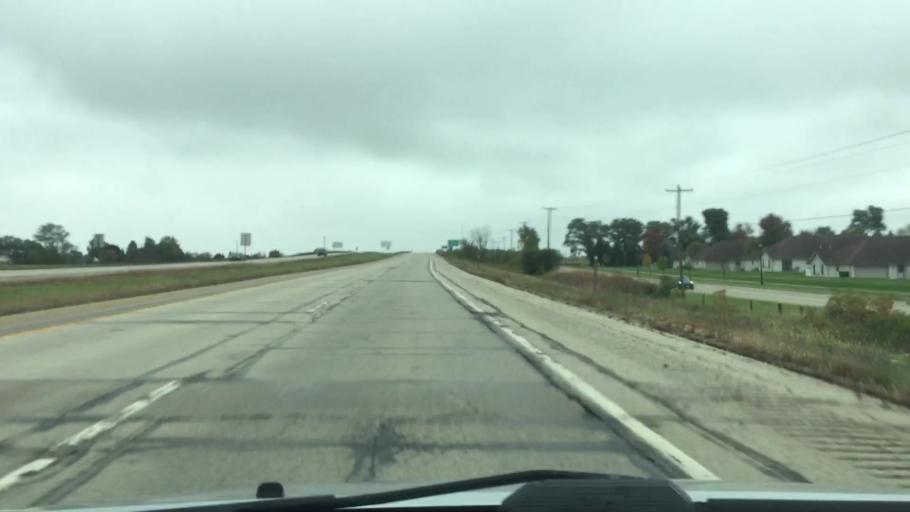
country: US
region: Wisconsin
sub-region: Walworth County
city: Elkhorn
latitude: 42.6870
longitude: -88.5309
